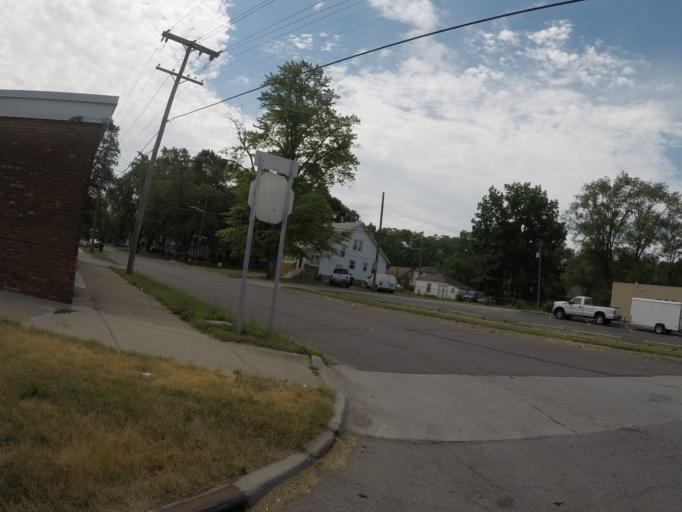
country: US
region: Michigan
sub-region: Wayne County
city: Redford
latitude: 42.4258
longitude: -83.2814
